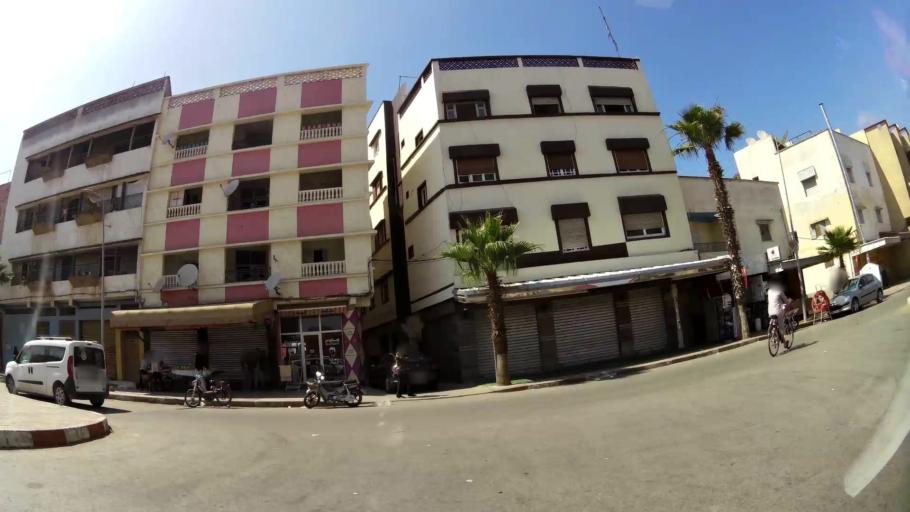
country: MA
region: Rabat-Sale-Zemmour-Zaer
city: Sale
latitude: 34.0642
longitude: -6.7684
